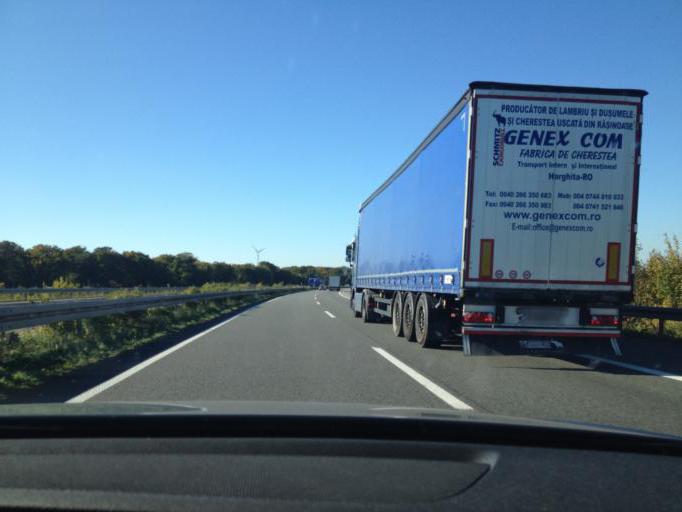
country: DE
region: Saarland
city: Orscholz
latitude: 49.4536
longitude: 6.4857
